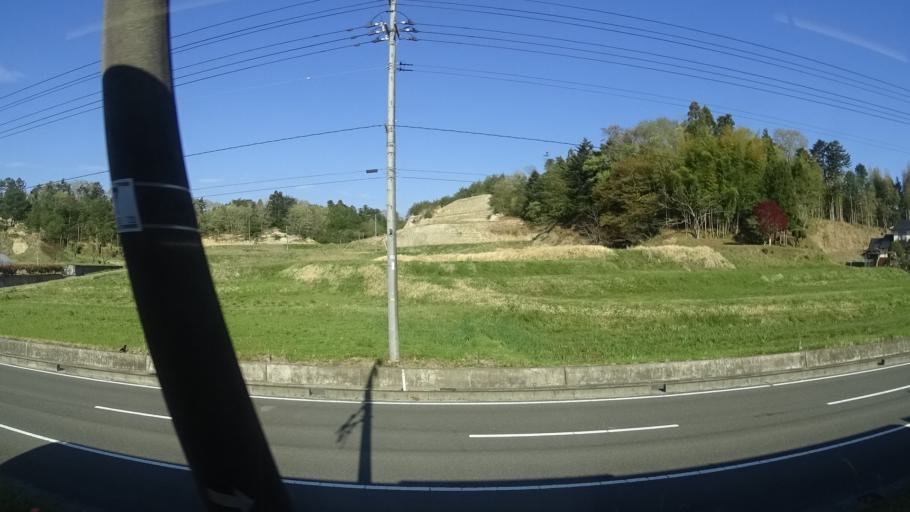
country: JP
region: Fukushima
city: Namie
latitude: 37.5501
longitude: 140.9939
